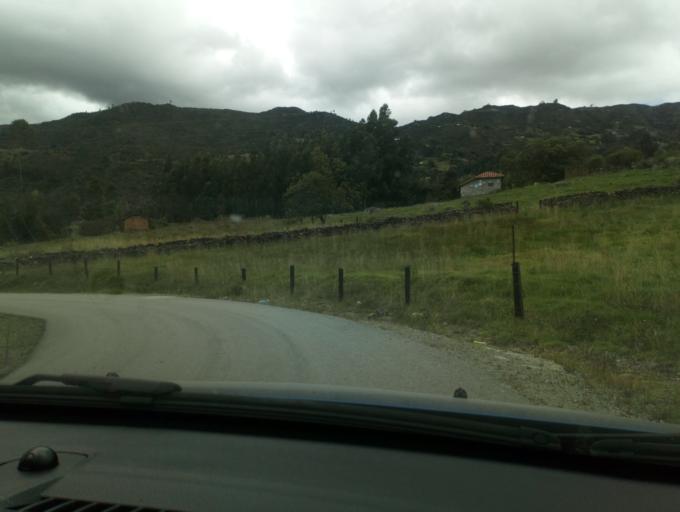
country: CO
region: Boyaca
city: Susacon
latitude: 6.1327
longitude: -72.6995
